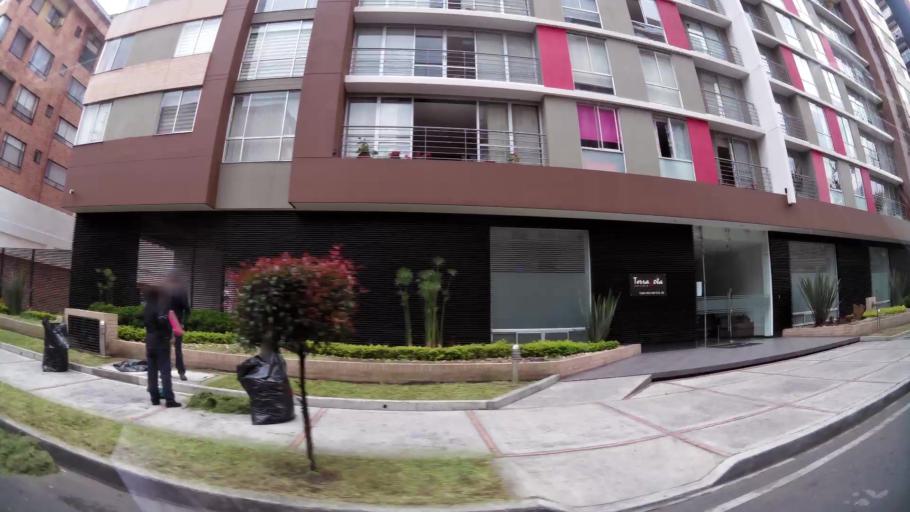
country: CO
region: Bogota D.C.
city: Barrio San Luis
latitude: 4.7250
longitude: -74.0365
